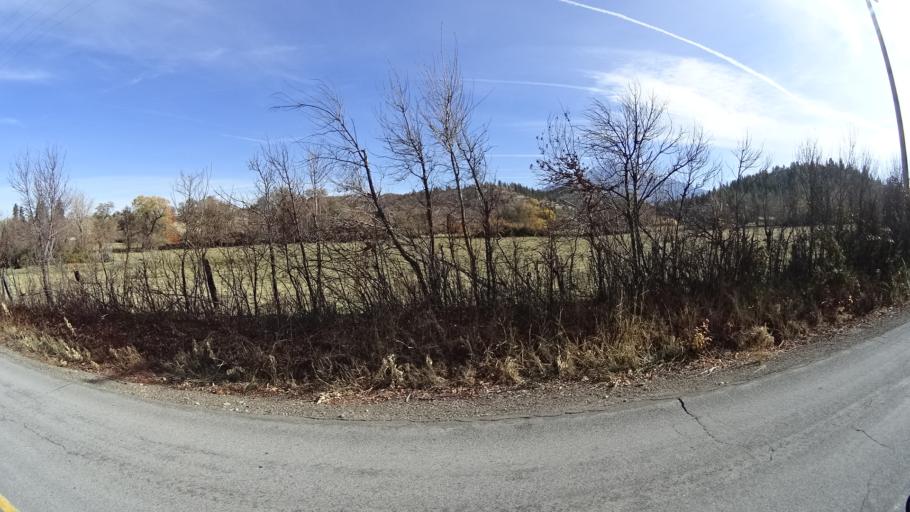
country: US
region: California
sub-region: Siskiyou County
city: Weed
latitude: 41.4542
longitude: -122.4313
